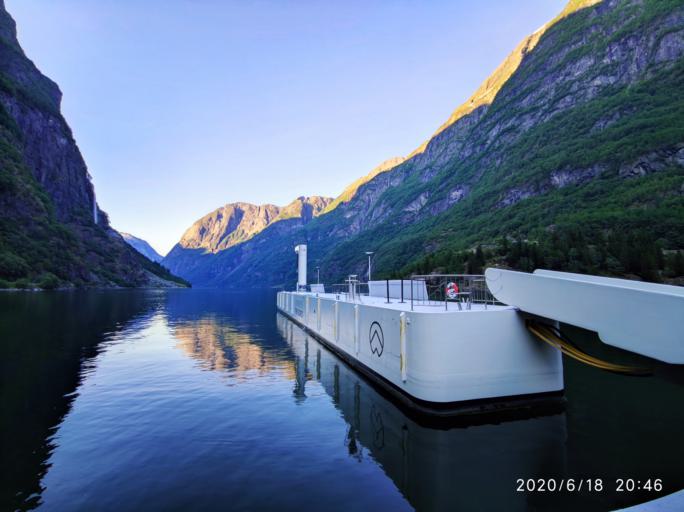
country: NO
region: Sogn og Fjordane
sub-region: Leikanger
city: Hermansverk
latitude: 60.8813
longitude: 6.8416
